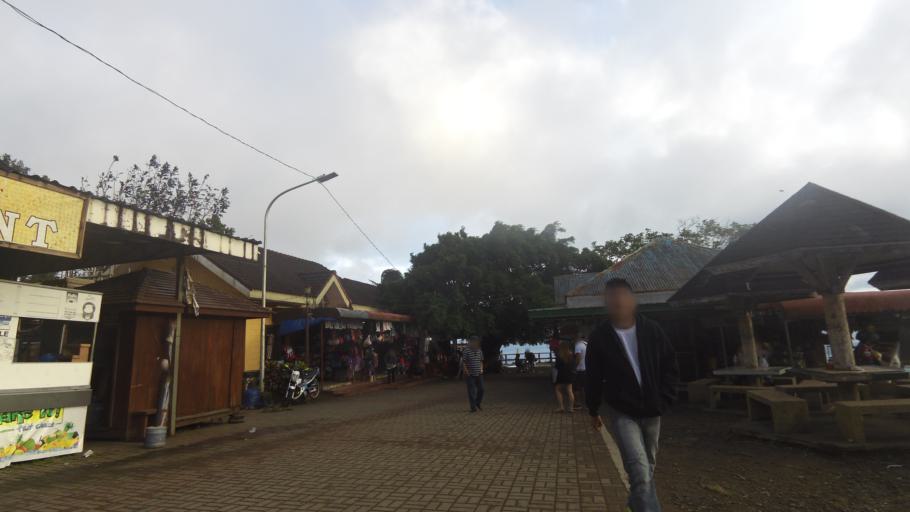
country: PH
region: Calabarzon
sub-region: Province of Cavite
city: Patuto
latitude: 14.1244
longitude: 120.9981
